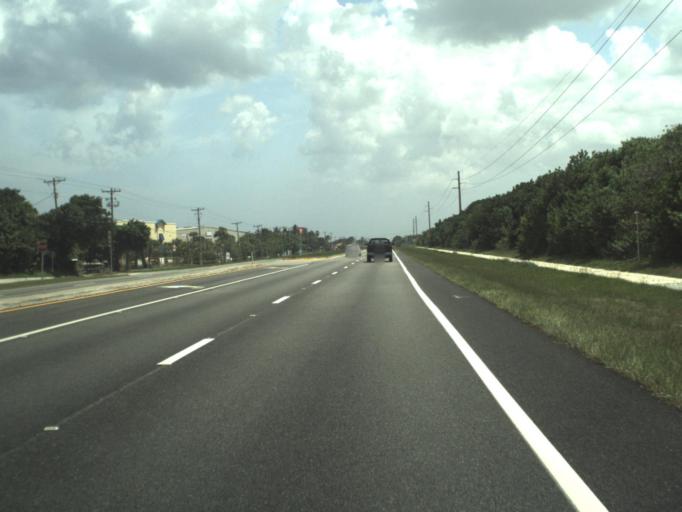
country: US
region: Florida
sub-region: Palm Beach County
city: Tequesta
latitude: 26.9788
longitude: -80.0902
